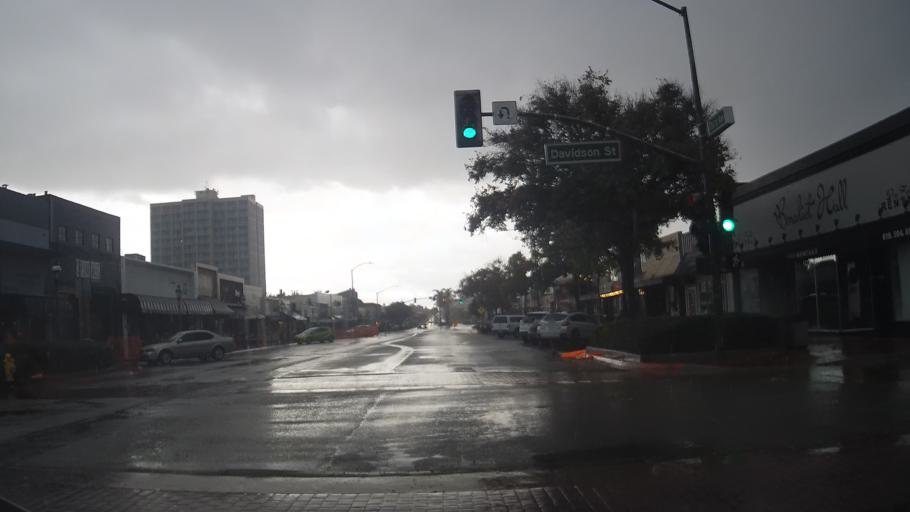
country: US
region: California
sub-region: San Diego County
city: Chula Vista
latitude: 32.6431
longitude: -117.0807
